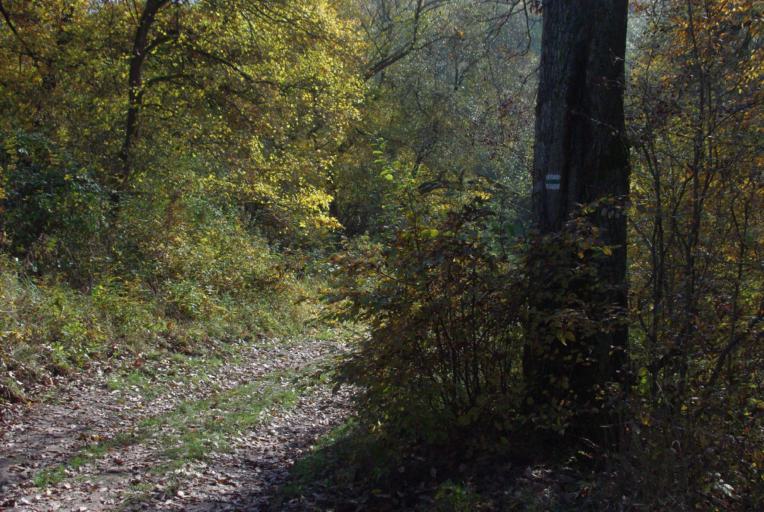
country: HU
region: Pest
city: Nagymaros
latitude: 47.8289
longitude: 18.9234
